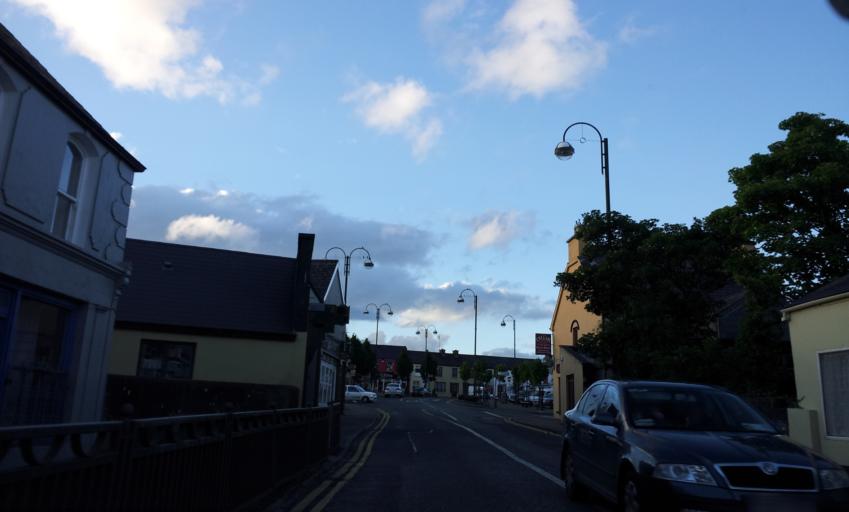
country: IE
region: Munster
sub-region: County Limerick
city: Abbeyfeale
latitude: 52.3837
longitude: -9.3017
